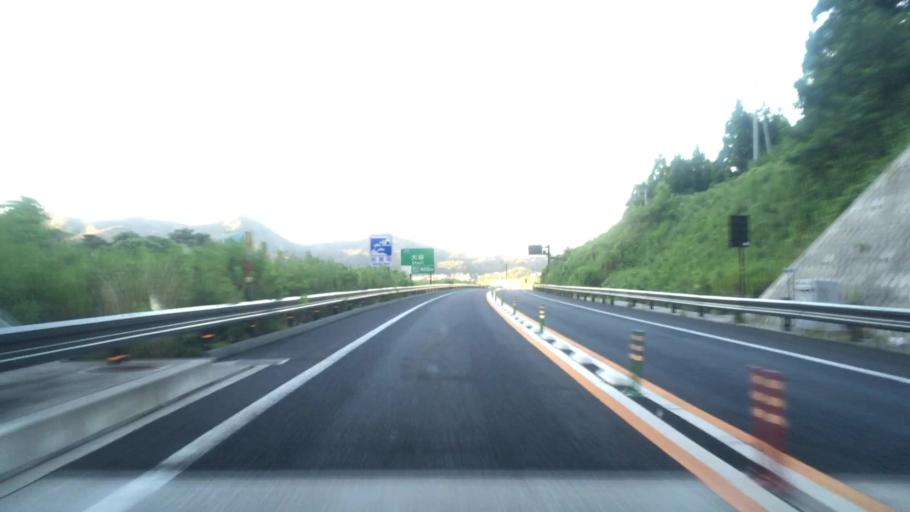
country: JP
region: Tottori
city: Tottori
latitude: 35.5673
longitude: 134.2916
